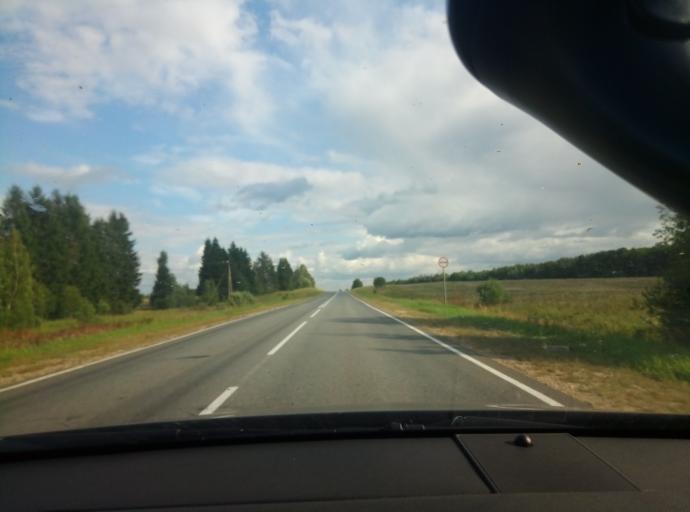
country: RU
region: Kaluga
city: Yukhnov
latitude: 54.6151
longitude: 35.3539
